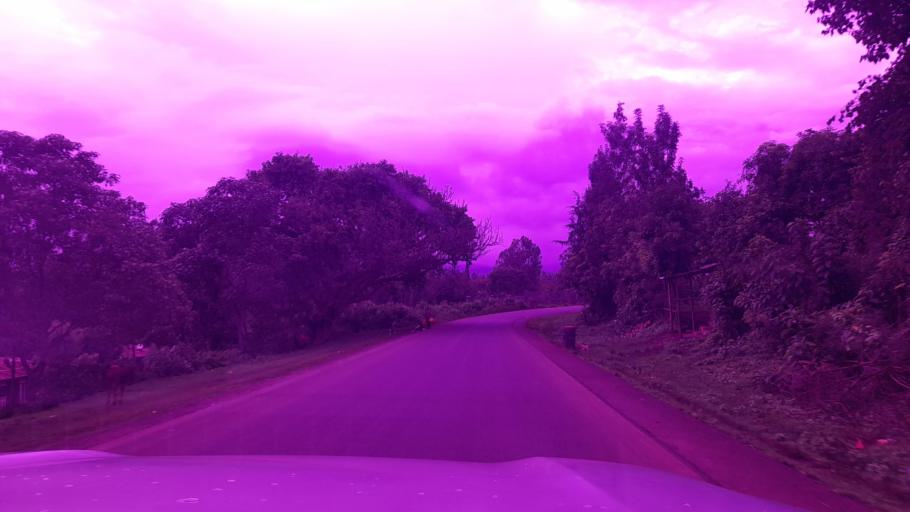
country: ET
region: Oromiya
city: Jima
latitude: 7.8924
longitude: 37.3880
